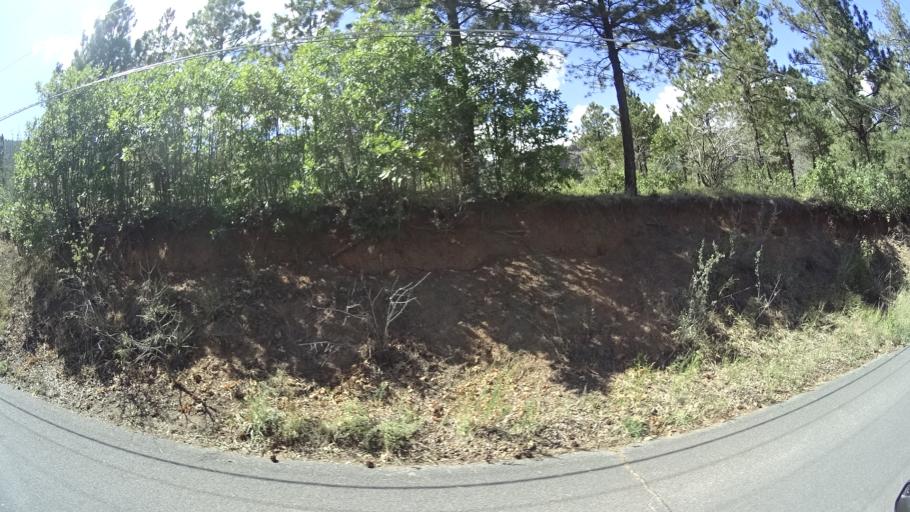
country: US
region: Colorado
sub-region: El Paso County
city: Colorado Springs
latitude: 38.7846
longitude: -104.8637
